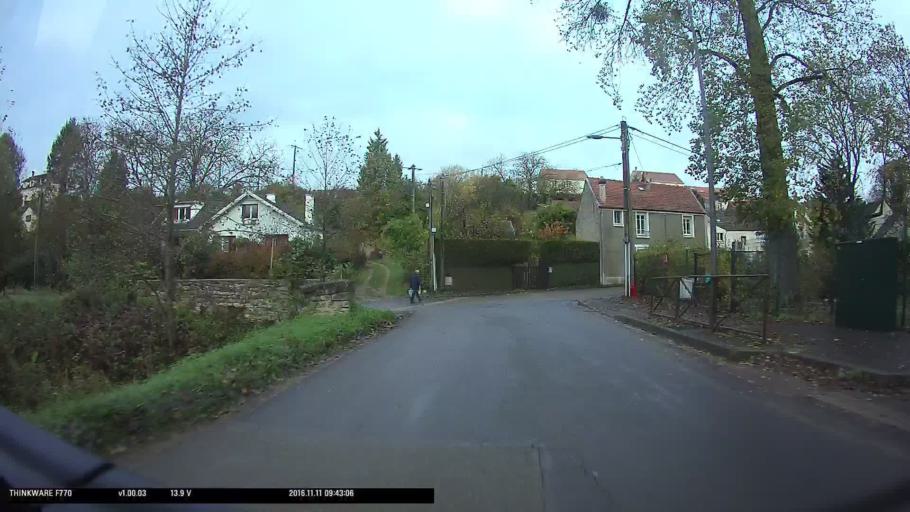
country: FR
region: Ile-de-France
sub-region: Departement du Val-d'Oise
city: Osny
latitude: 49.0670
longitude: 2.0506
